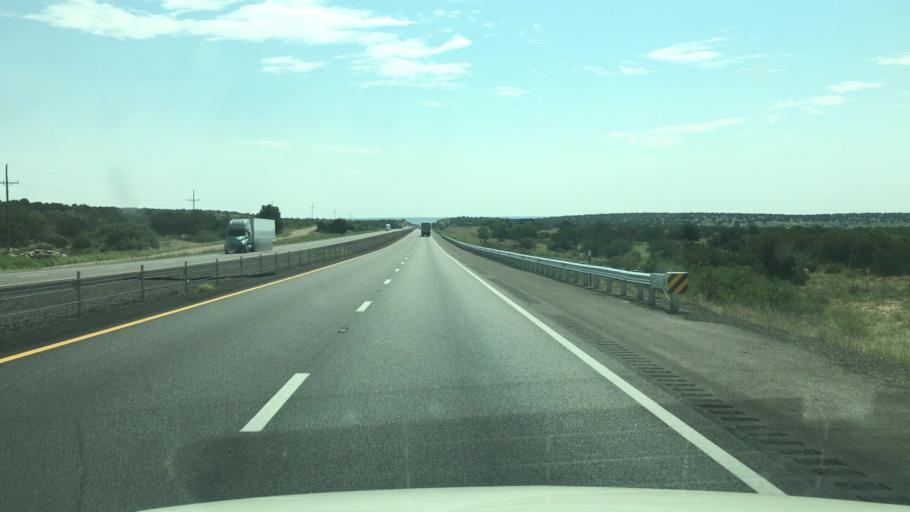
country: US
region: New Mexico
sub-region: Guadalupe County
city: Santa Rosa
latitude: 34.9659
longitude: -104.7621
